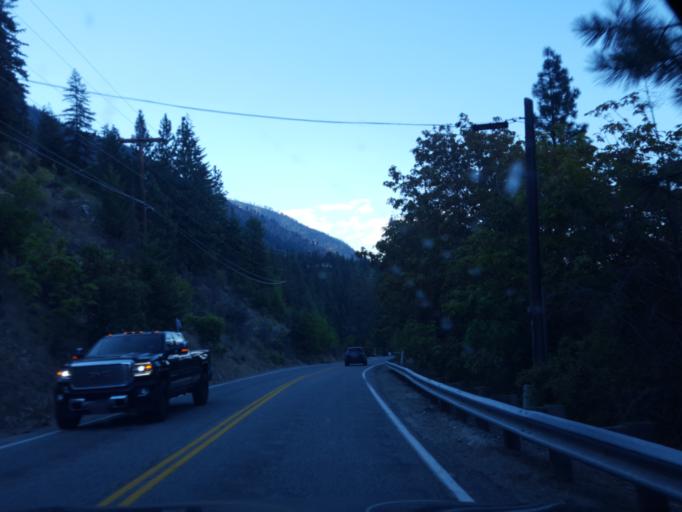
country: US
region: Washington
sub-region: Chelan County
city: Granite Falls
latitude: 47.9054
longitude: -120.2162
